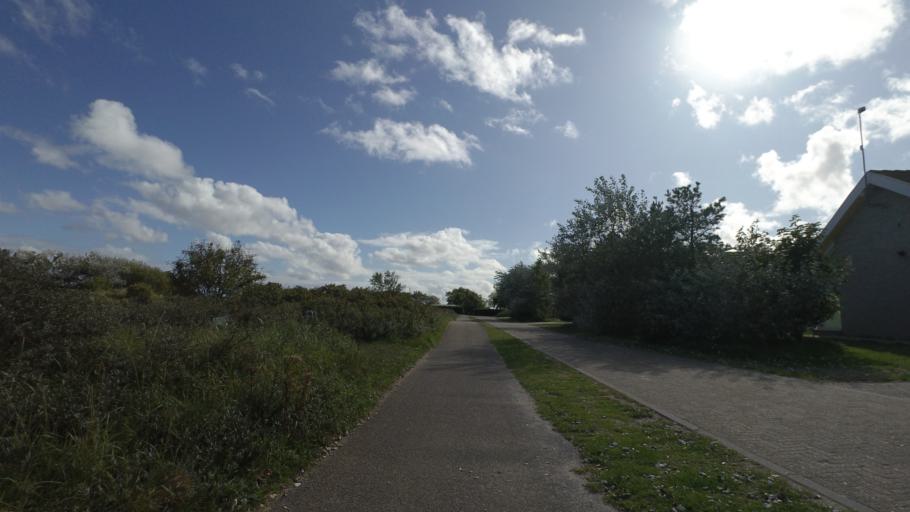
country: NL
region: Friesland
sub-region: Gemeente Ameland
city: Nes
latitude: 53.4546
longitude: 5.8143
